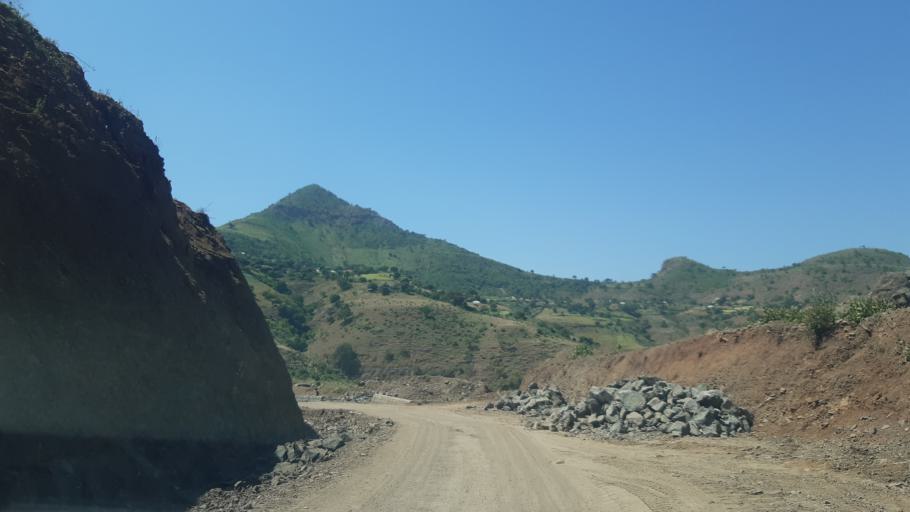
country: ET
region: Amhara
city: Dabat
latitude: 13.1691
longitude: 37.6055
